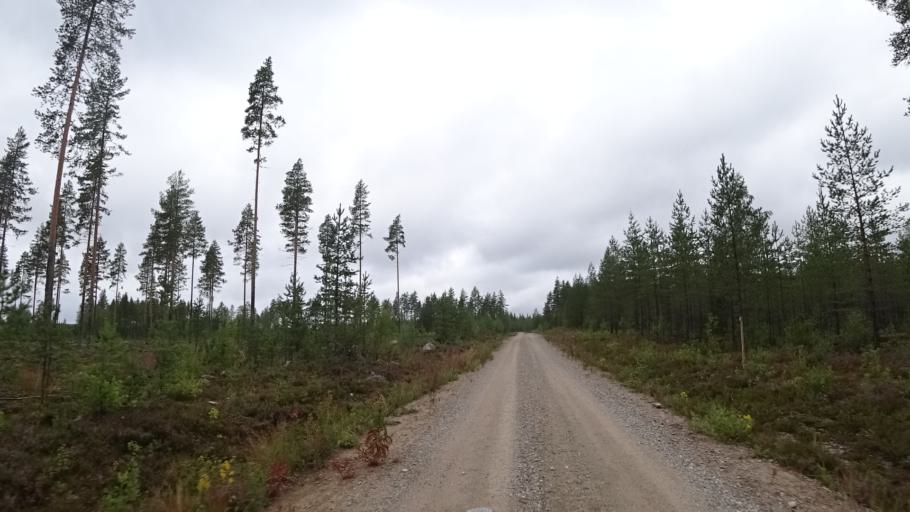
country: FI
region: North Karelia
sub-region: Pielisen Karjala
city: Lieksa
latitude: 63.5126
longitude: 30.1342
